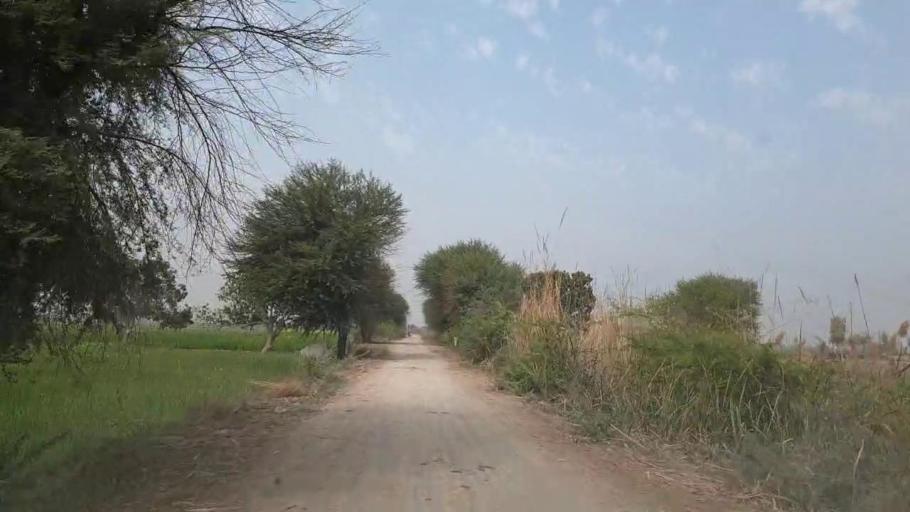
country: PK
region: Sindh
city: Mirpur Khas
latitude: 25.5603
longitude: 69.1071
